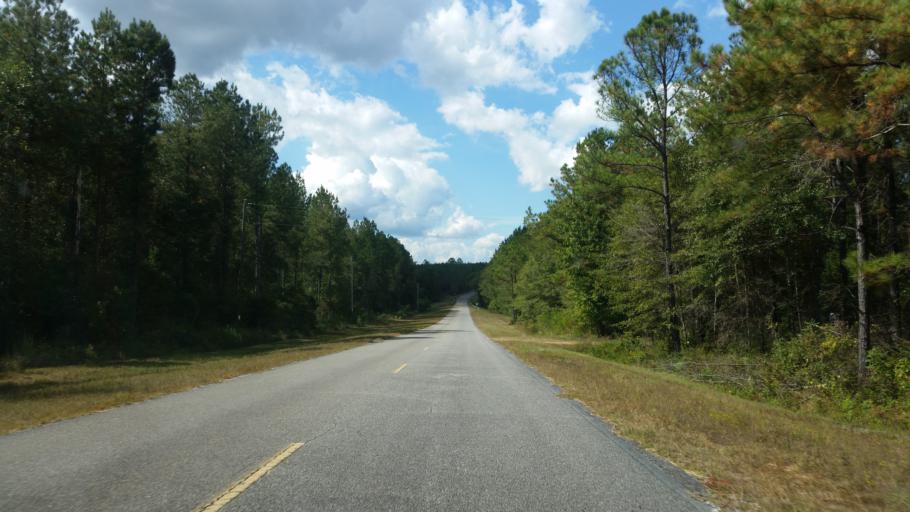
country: US
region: Alabama
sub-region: Escambia County
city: Atmore
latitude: 30.8884
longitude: -87.5366
